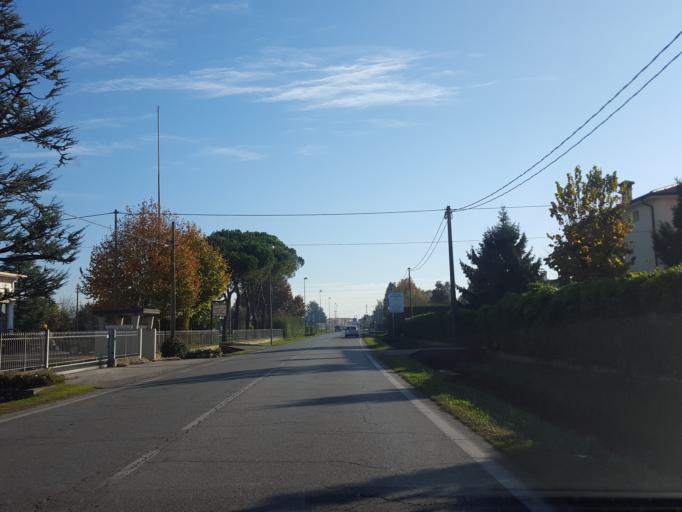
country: IT
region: Veneto
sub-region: Provincia di Vicenza
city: Grumolo delle Abbadesse
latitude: 45.5210
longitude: 11.6835
